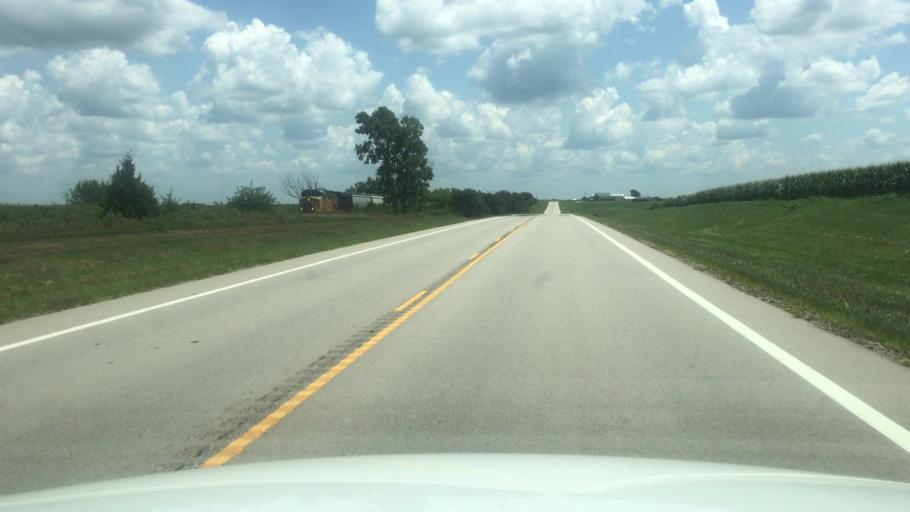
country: US
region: Kansas
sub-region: Brown County
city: Horton
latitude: 39.6565
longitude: -95.3729
